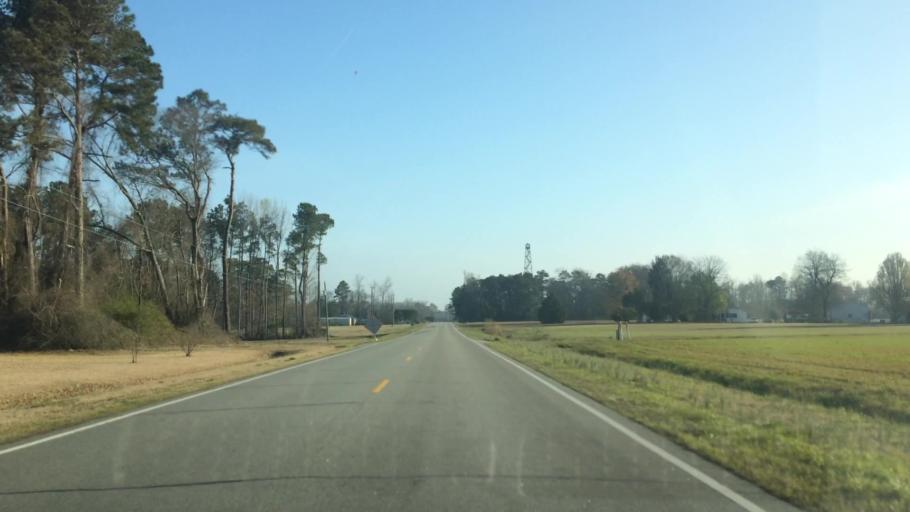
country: US
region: North Carolina
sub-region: Edgecombe County
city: Pinetops
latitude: 35.6922
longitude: -77.6402
